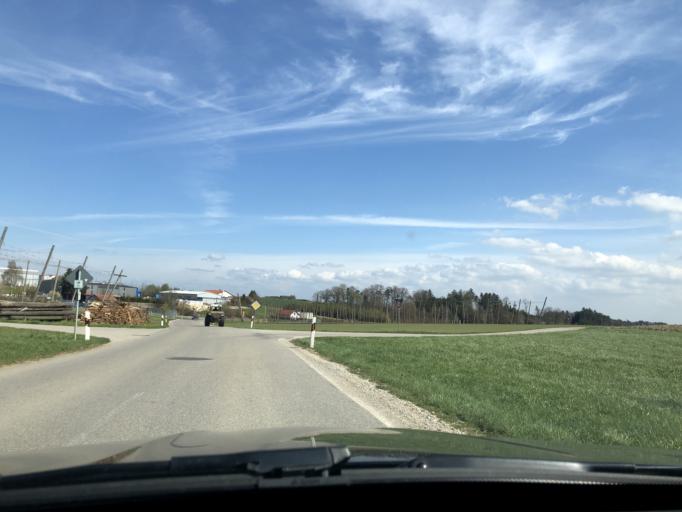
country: DE
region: Bavaria
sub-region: Upper Bavaria
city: Schweitenkirchen
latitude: 48.4996
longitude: 11.5980
